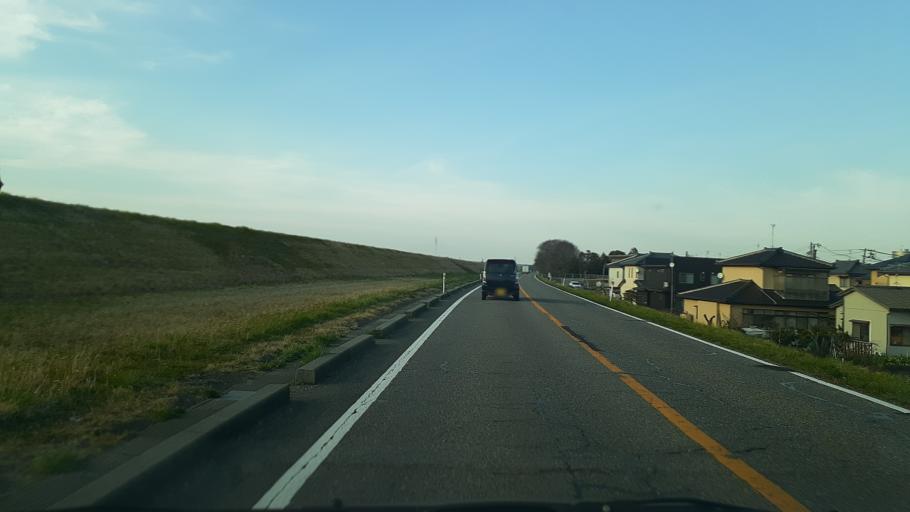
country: JP
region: Niigata
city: Niigata-shi
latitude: 37.8581
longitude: 139.0245
